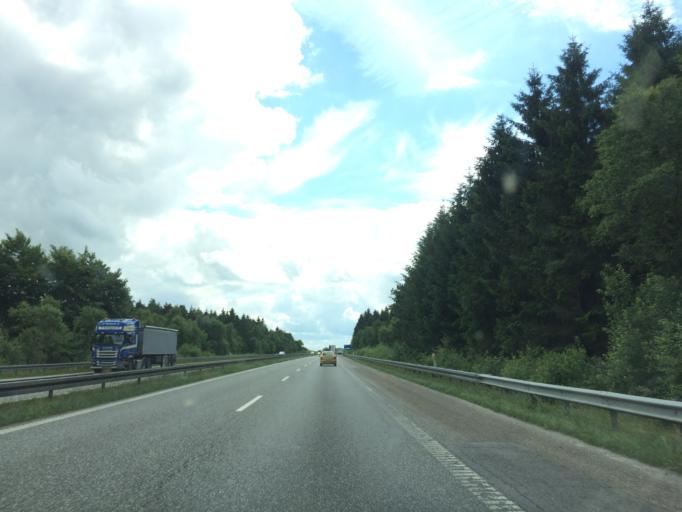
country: DK
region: North Denmark
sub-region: Mariagerfjord Kommune
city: Hobro
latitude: 56.6408
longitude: 9.7370
